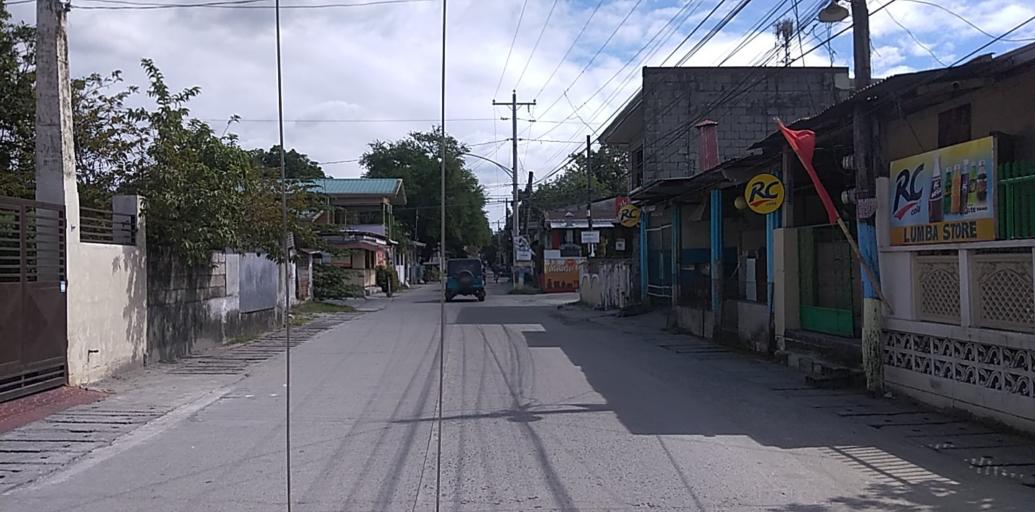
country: PH
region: Central Luzon
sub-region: Province of Pampanga
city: Porac
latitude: 15.0705
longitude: 120.5422
